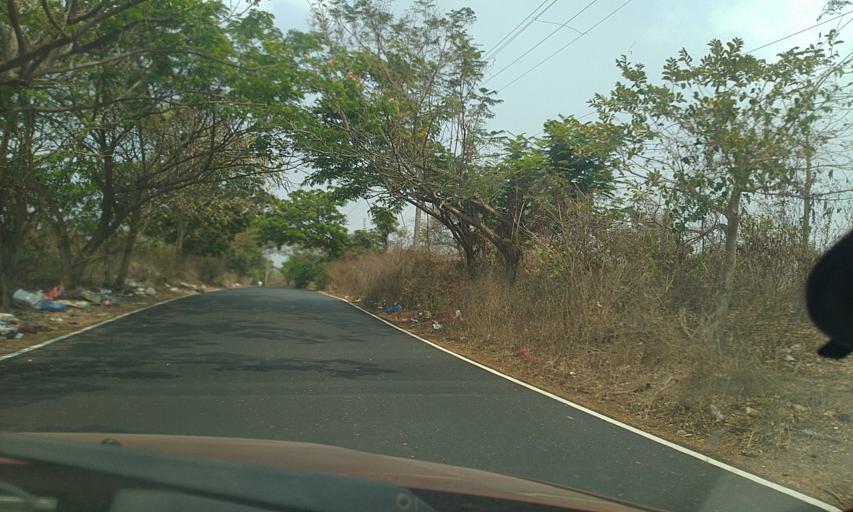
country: IN
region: Goa
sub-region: North Goa
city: Mapuca
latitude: 15.6075
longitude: 73.8006
